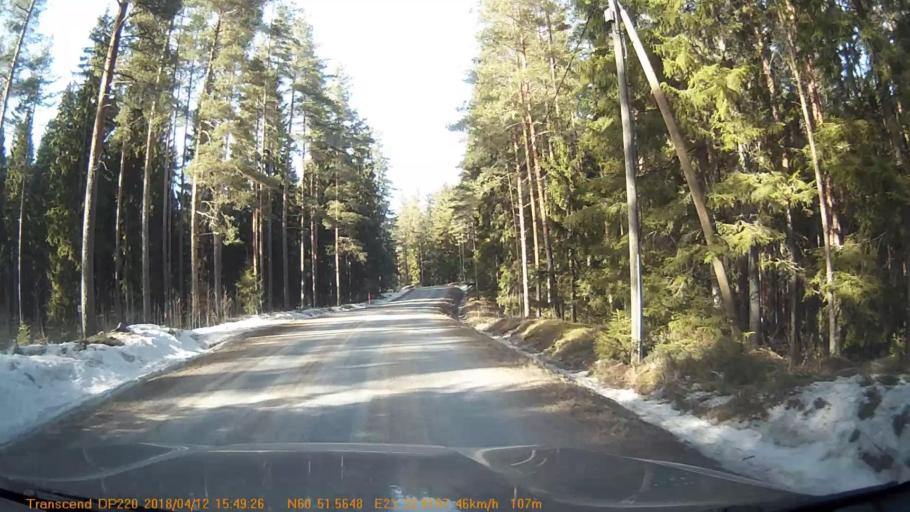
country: FI
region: Haeme
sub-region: Forssa
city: Forssa
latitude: 60.8596
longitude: 23.5486
